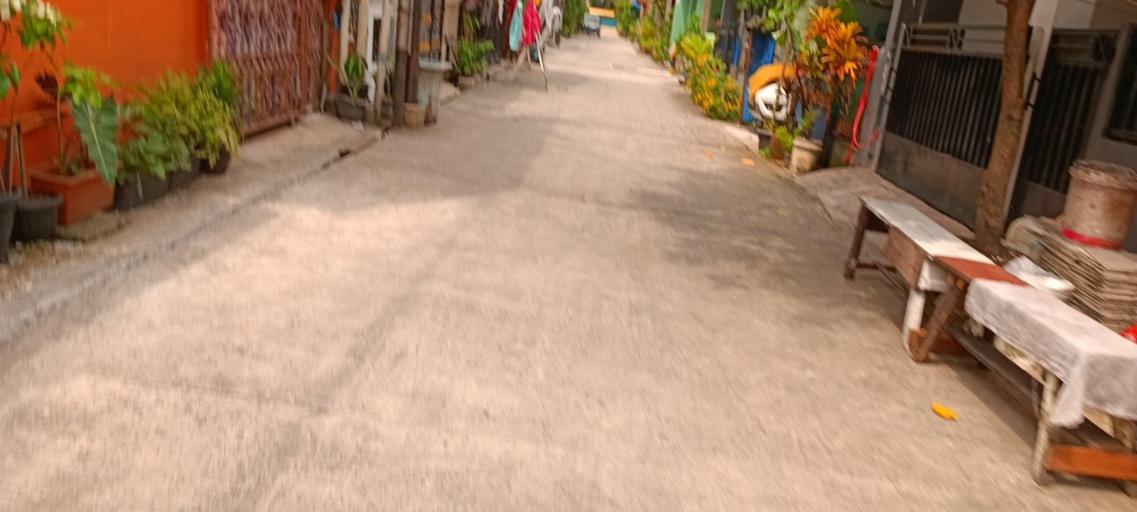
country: ID
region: West Java
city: Pamulang
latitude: -6.3596
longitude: 106.7307
